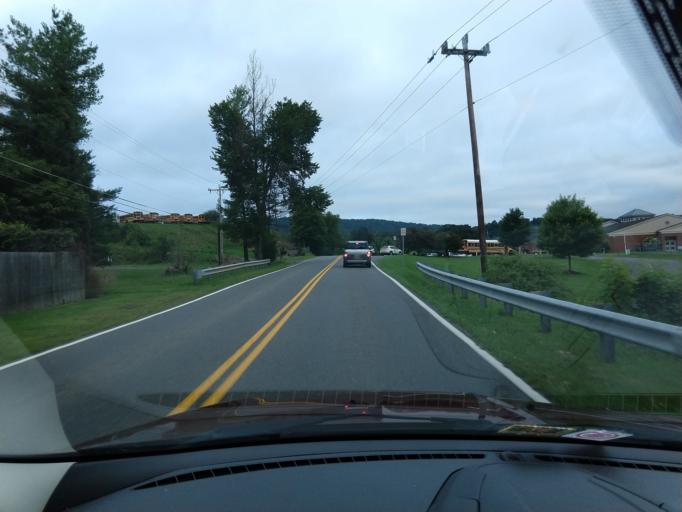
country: US
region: Virginia
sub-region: City of Covington
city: Fairlawn
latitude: 37.7523
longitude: -79.9931
